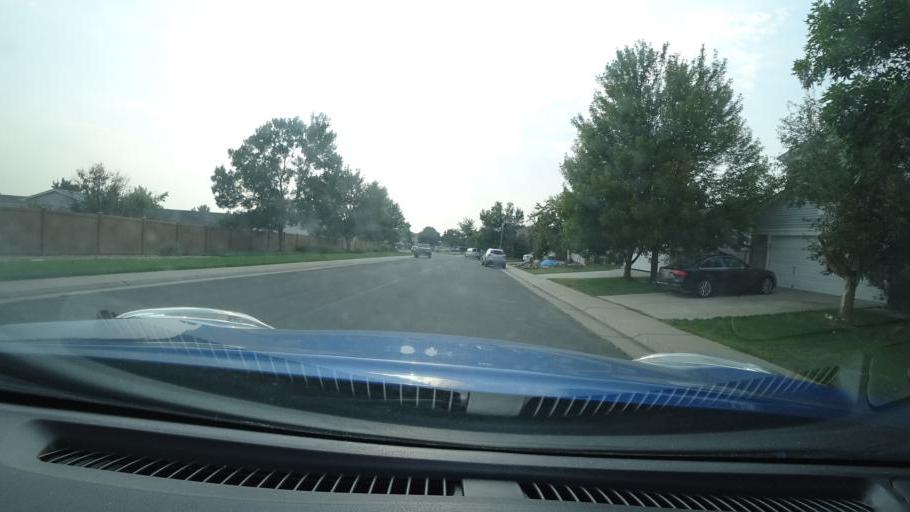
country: US
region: Colorado
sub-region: Adams County
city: Aurora
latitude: 39.7470
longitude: -104.7593
